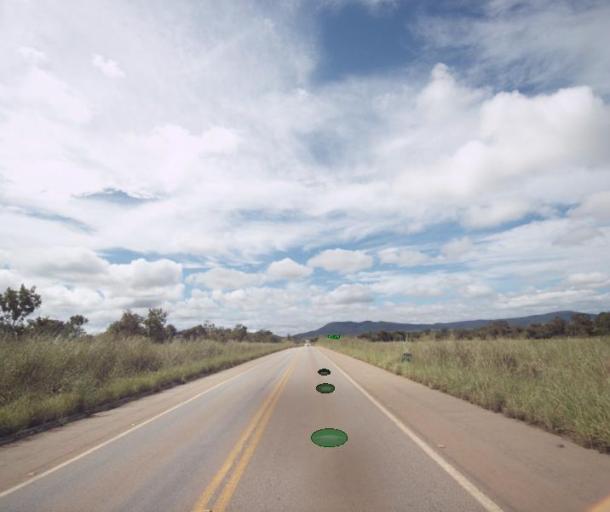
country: BR
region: Goias
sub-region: Barro Alto
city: Barro Alto
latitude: -15.1797
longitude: -48.7896
